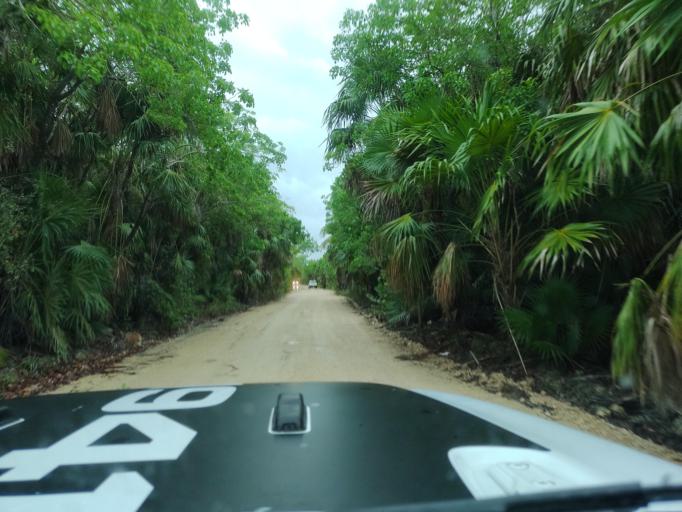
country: MX
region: Quintana Roo
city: Tulum
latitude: 20.0621
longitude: -87.4806
